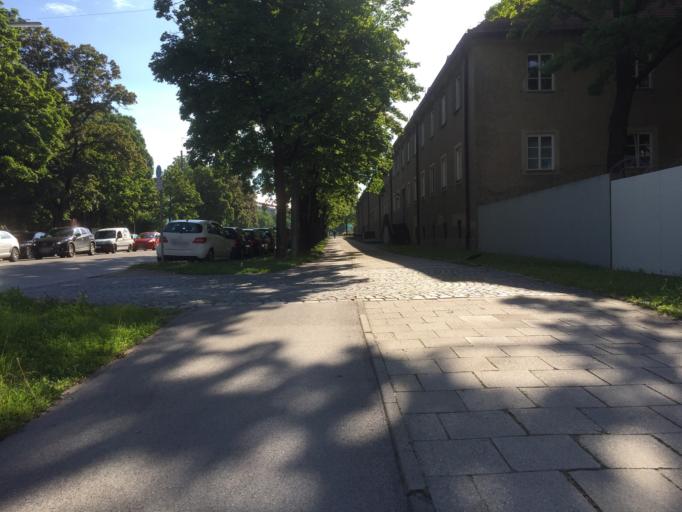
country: DE
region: Bavaria
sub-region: Upper Bavaria
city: Munich
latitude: 48.1200
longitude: 11.6030
